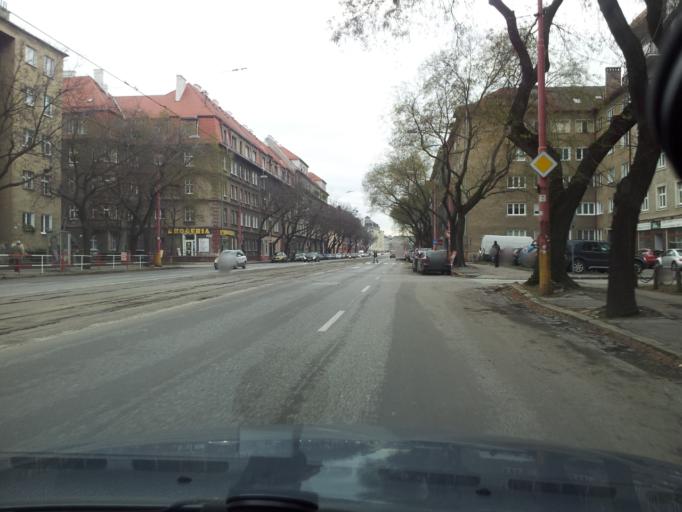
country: SK
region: Bratislavsky
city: Bratislava
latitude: 48.1613
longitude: 17.1310
